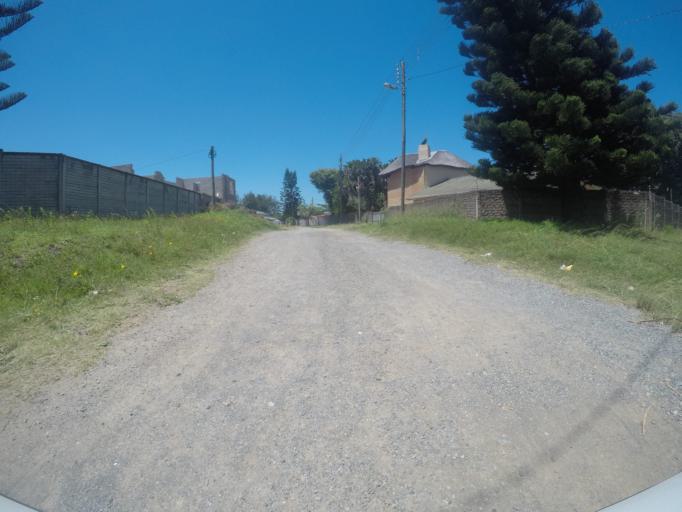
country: ZA
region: Eastern Cape
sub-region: Buffalo City Metropolitan Municipality
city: East London
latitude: -32.9546
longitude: 28.0008
